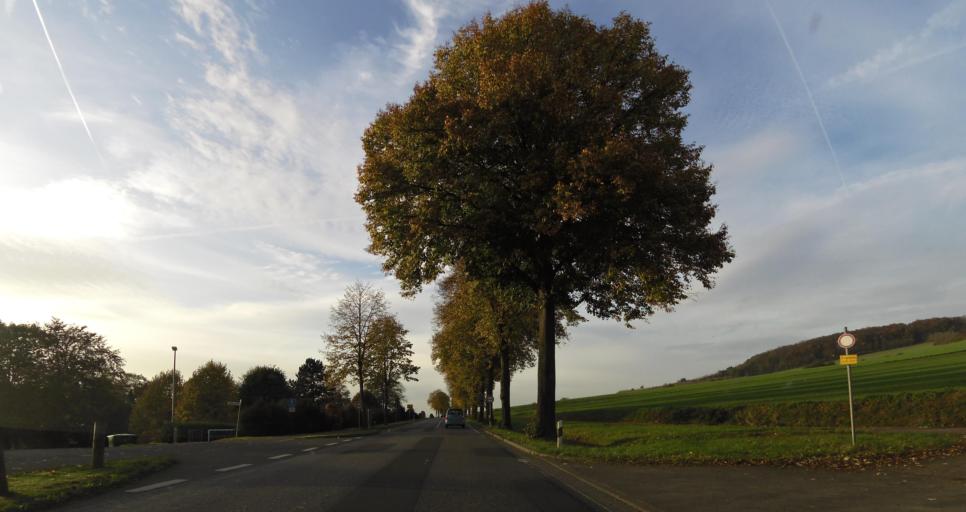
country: DE
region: Lower Saxony
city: Northeim
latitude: 51.7665
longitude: 9.9564
